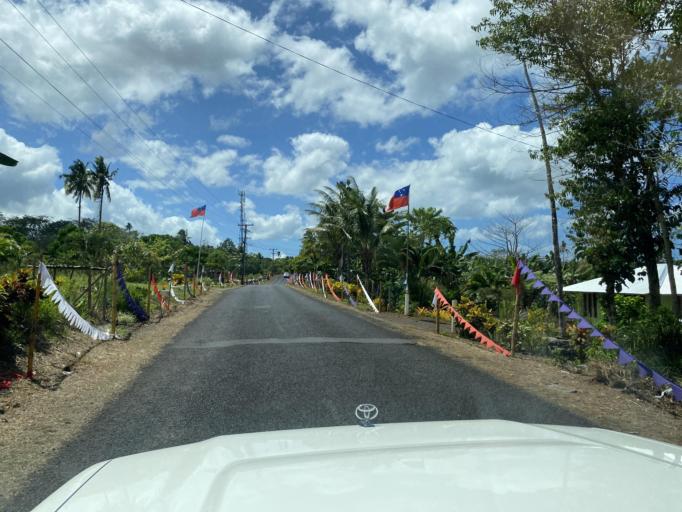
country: WS
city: Lotofaga
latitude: -14.0049
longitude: -171.7904
